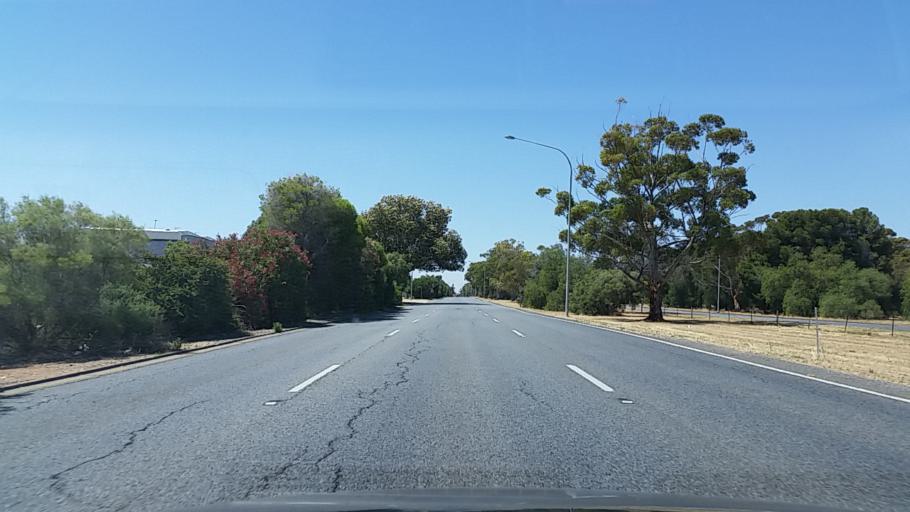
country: AU
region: South Australia
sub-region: Salisbury
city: Elizabeth
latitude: -34.7044
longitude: 138.6801
